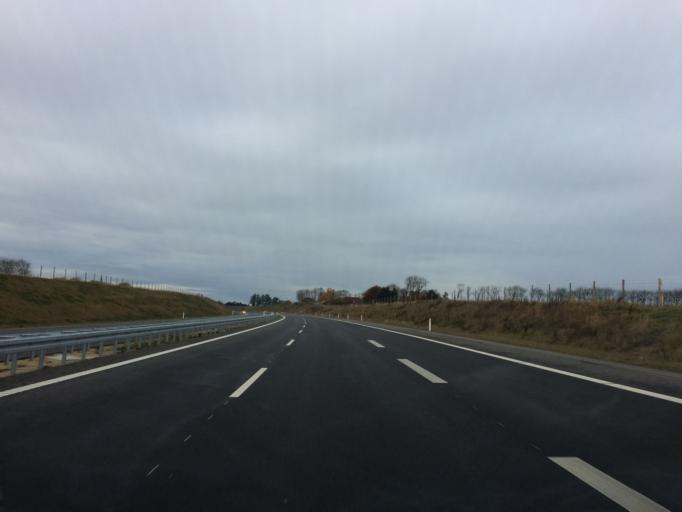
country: DK
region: Central Jutland
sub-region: Silkeborg Kommune
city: Silkeborg
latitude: 56.2033
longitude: 9.5441
